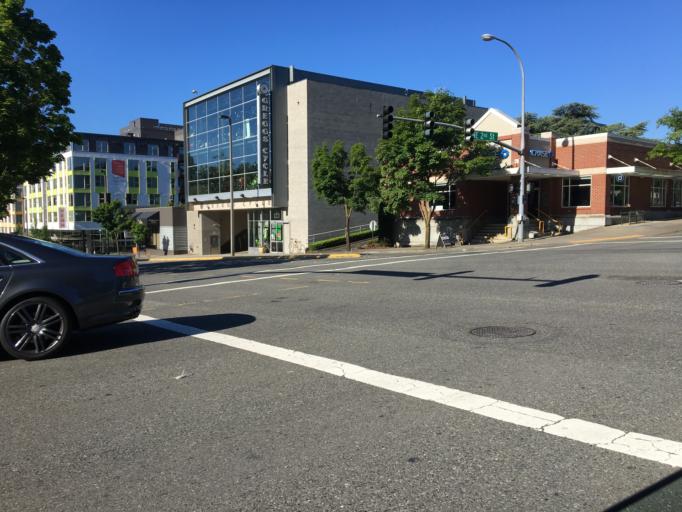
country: US
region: Washington
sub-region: King County
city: Bellevue
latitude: 47.6121
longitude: -122.2013
